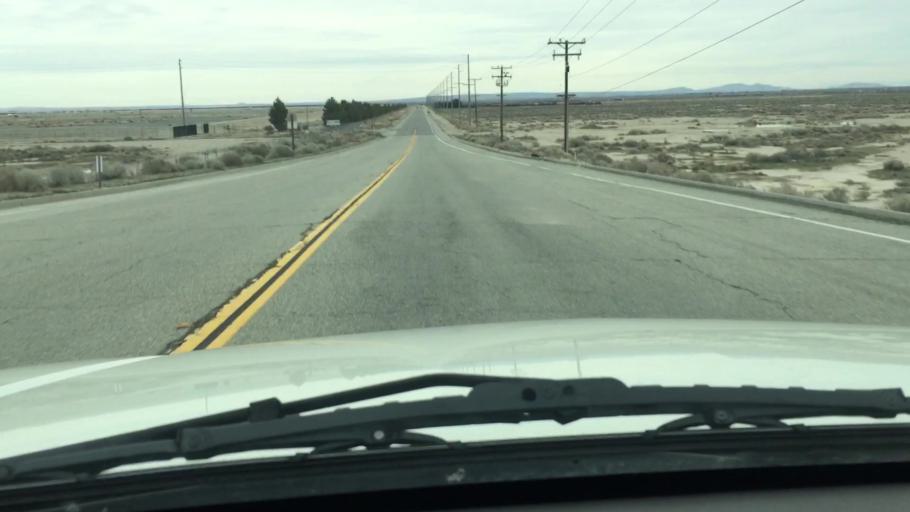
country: US
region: California
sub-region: Los Angeles County
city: Lancaster
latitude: 34.7769
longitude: -118.1686
